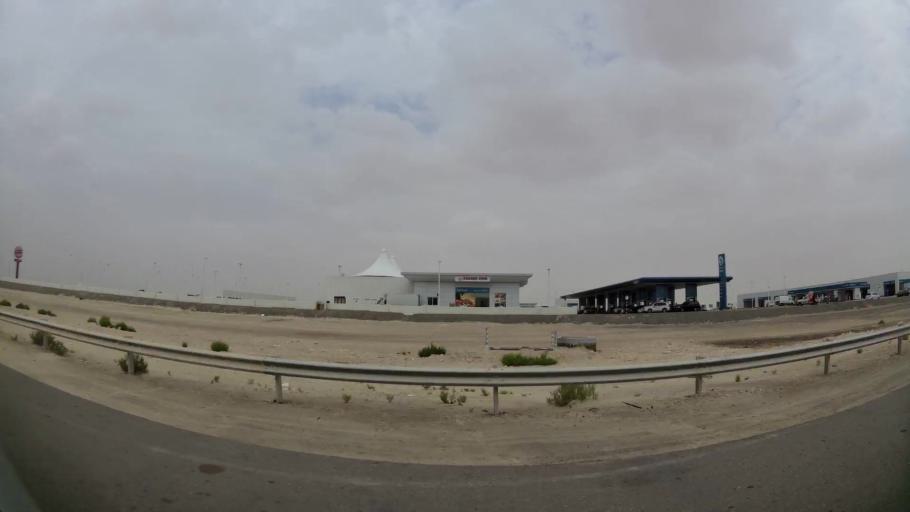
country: AE
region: Abu Dhabi
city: Abu Dhabi
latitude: 24.3976
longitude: 54.6904
